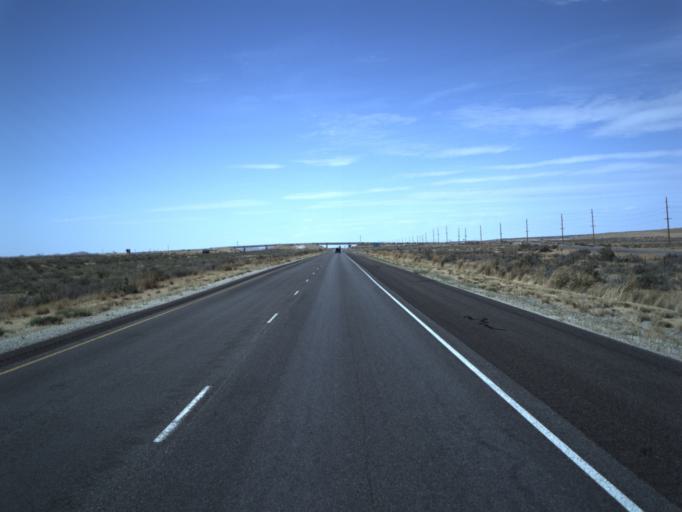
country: US
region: Utah
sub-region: Tooele County
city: Grantsville
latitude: 40.7356
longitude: -113.1024
